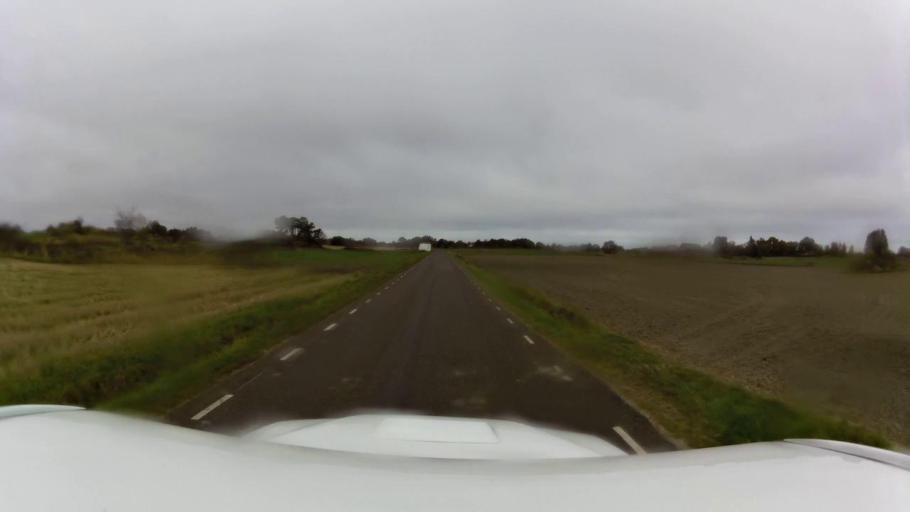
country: SE
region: OEstergoetland
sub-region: Linkopings Kommun
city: Linghem
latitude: 58.4816
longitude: 15.7452
